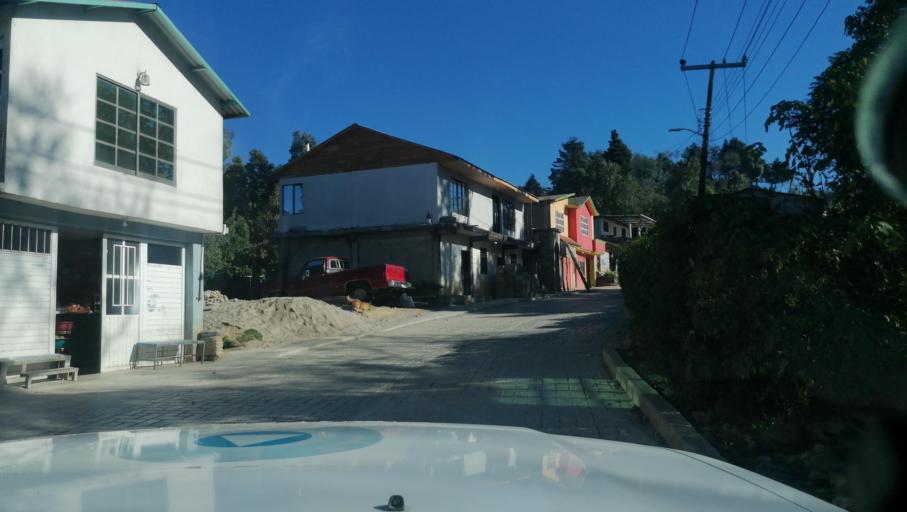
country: MX
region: Chiapas
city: Motozintla de Mendoza
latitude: 15.2569
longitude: -92.2131
